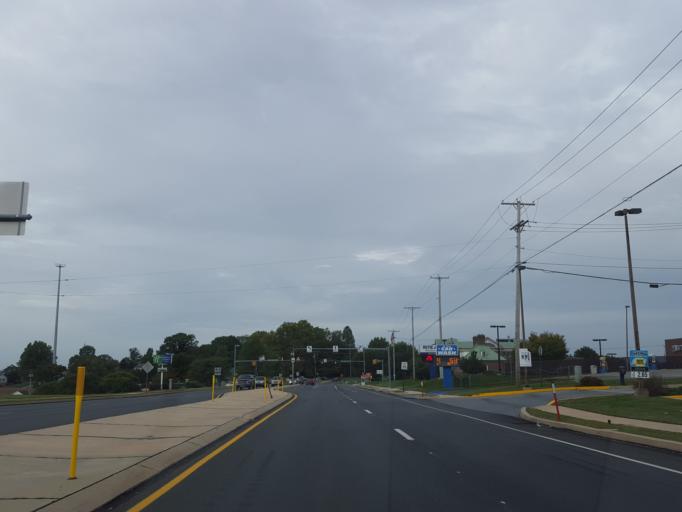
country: US
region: Pennsylvania
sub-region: York County
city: Spry
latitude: 39.9101
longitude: -76.7046
